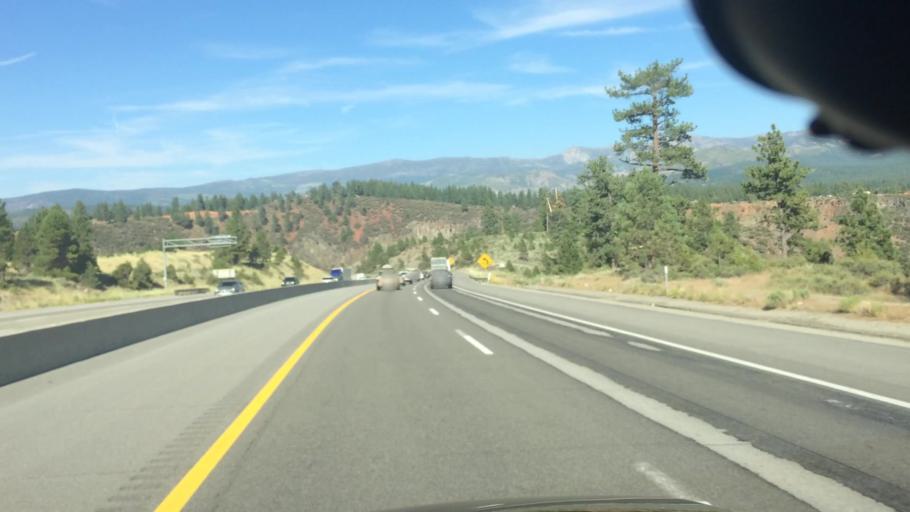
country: US
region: California
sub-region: Nevada County
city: Truckee
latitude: 39.3635
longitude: -120.1230
